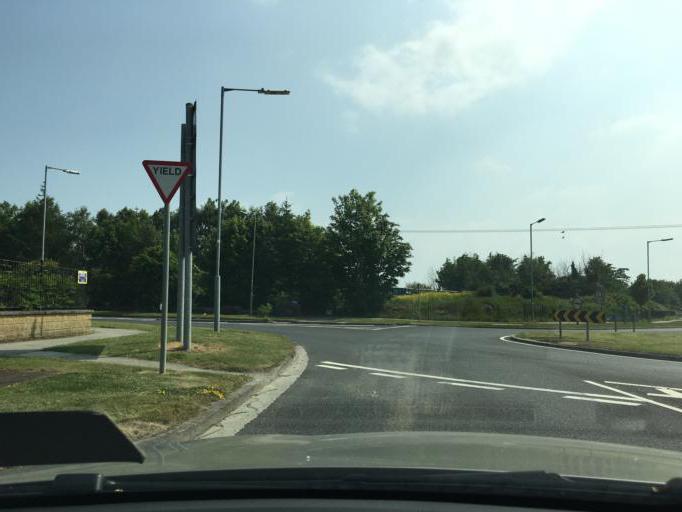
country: IE
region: Leinster
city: Hartstown
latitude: 53.4094
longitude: -6.4094
